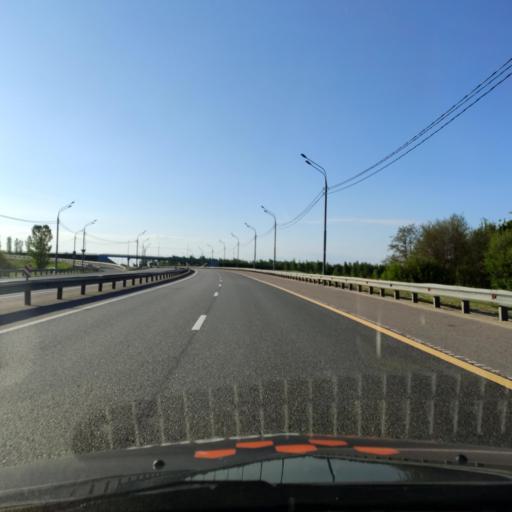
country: RU
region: Lipetsk
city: Khlevnoye
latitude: 52.2409
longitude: 39.0691
